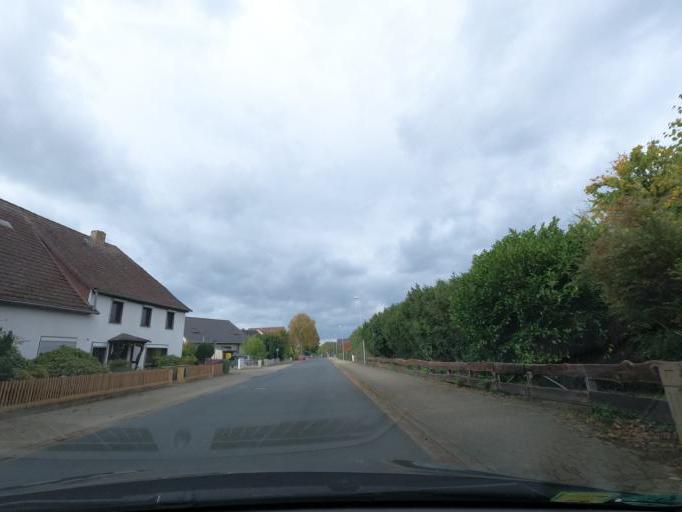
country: DE
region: Lower Saxony
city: Klein Schwulper
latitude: 52.3364
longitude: 10.4363
